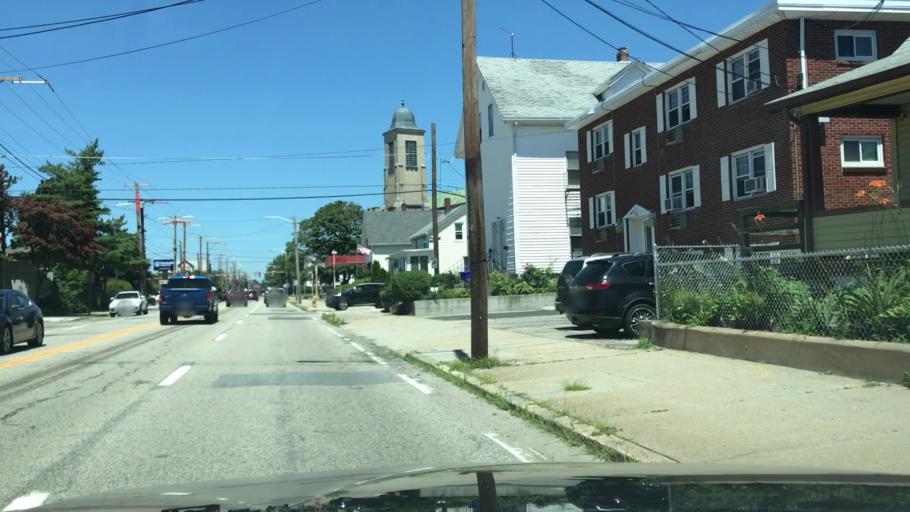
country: US
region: Massachusetts
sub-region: Bristol County
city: North Seekonk
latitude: 41.8860
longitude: -71.3541
